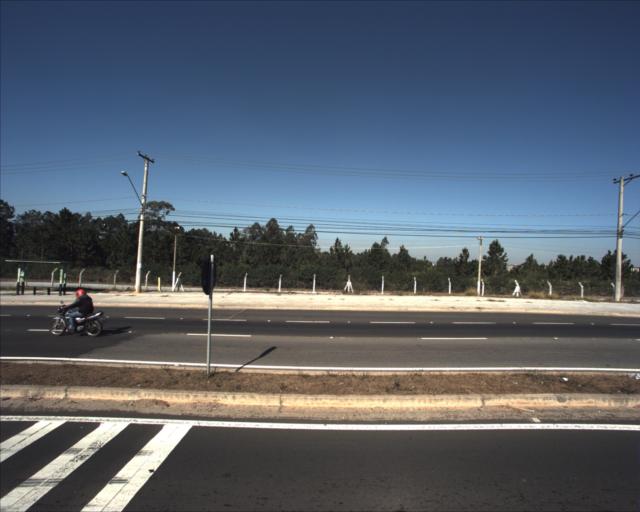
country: BR
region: Sao Paulo
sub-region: Sorocaba
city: Sorocaba
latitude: -23.4117
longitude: -47.3877
